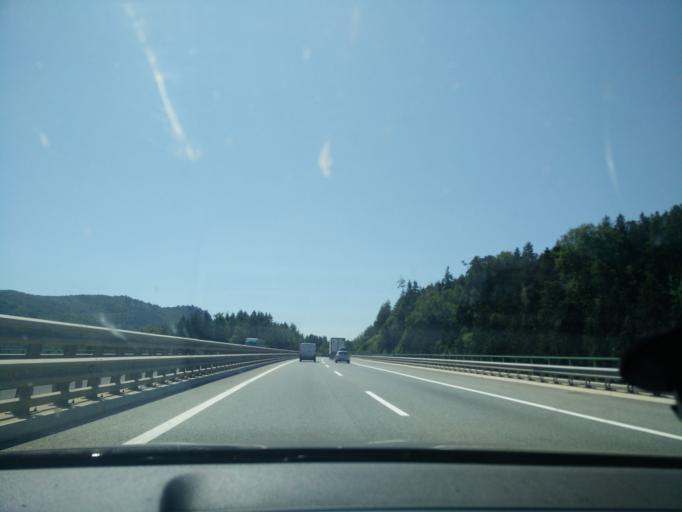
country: AT
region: Lower Austria
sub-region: Politischer Bezirk Neunkirchen
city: Seebenstein
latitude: 47.6987
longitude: 16.1303
